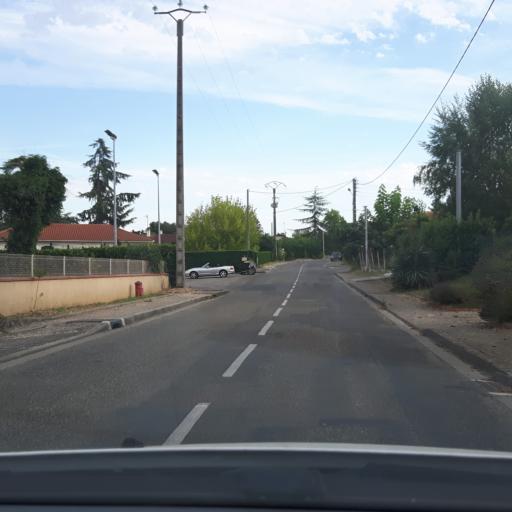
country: FR
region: Midi-Pyrenees
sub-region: Departement de la Haute-Garonne
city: Fronton
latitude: 43.8386
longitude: 1.3830
